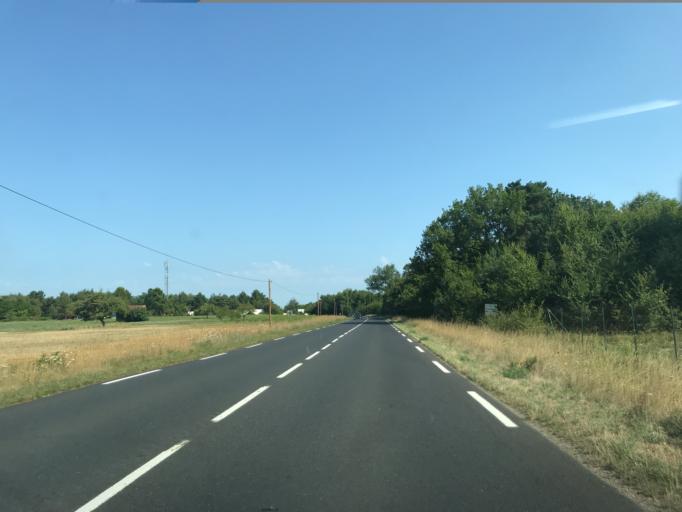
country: FR
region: Aquitaine
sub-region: Departement de la Dordogne
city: Montignac
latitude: 45.0272
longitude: 1.2291
